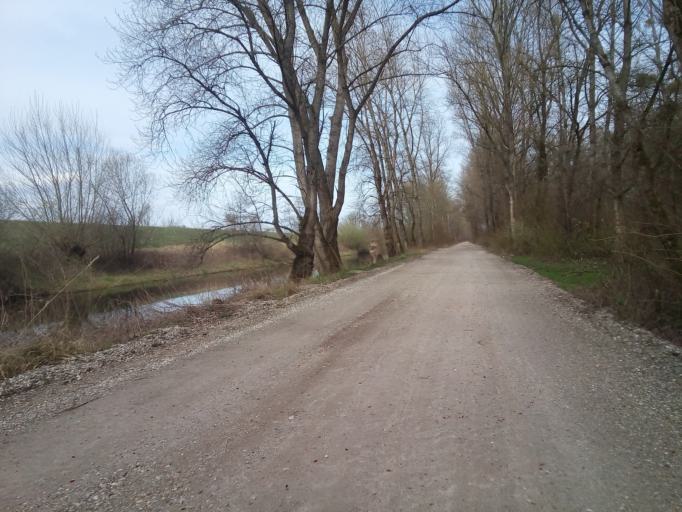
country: DE
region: Baden-Wuerttemberg
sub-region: Karlsruhe Region
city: Lichtenau
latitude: 48.7129
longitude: 7.9562
